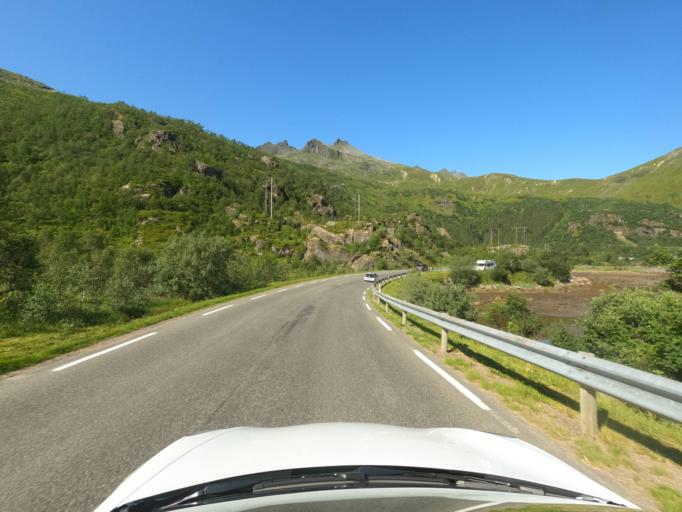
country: NO
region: Nordland
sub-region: Hadsel
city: Melbu
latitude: 68.3551
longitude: 14.7093
